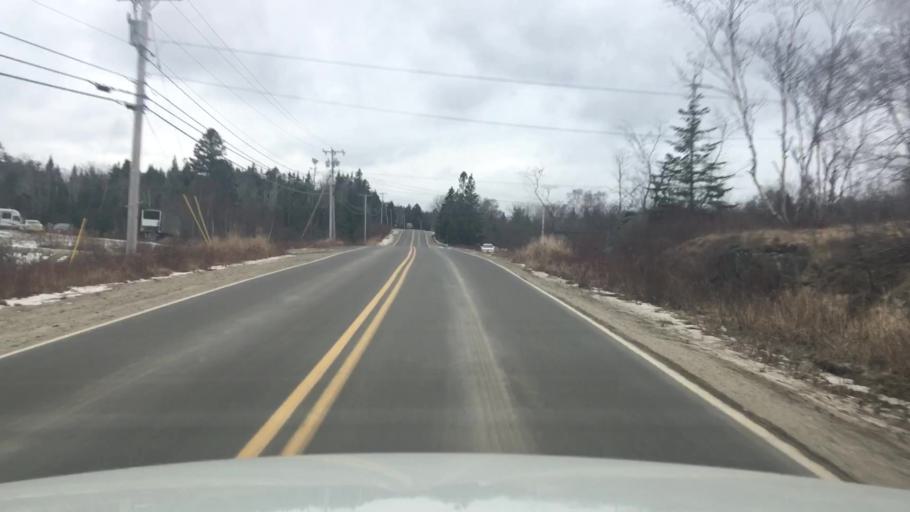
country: US
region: Maine
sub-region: Washington County
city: Jonesport
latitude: 44.5583
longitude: -67.6286
